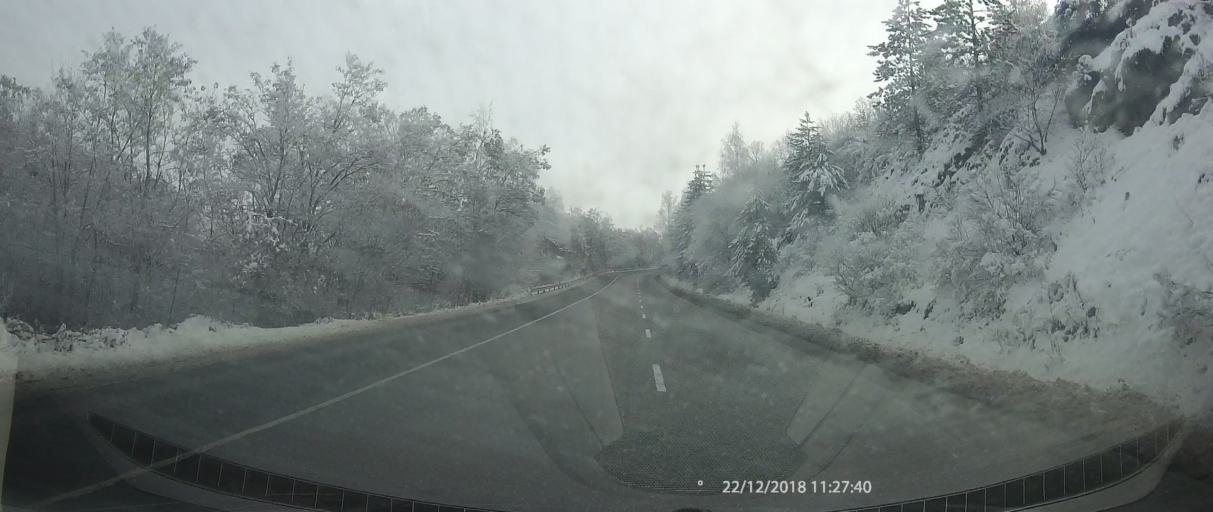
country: BG
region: Kyustendil
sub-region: Obshtina Bobovdol
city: Bobovdol
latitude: 42.2757
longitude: 22.9394
